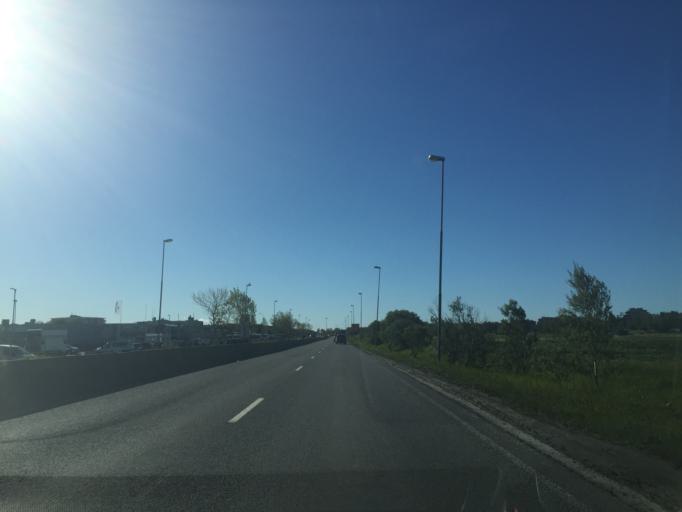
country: NO
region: Nordland
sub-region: Bodo
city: Bodo
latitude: 67.2792
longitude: 14.4288
